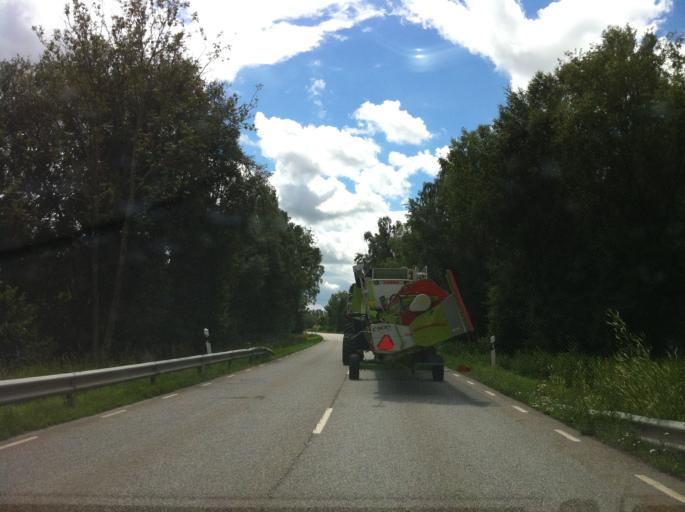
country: SE
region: Skane
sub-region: Svedala Kommun
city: Klagerup
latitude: 55.5840
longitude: 13.2535
